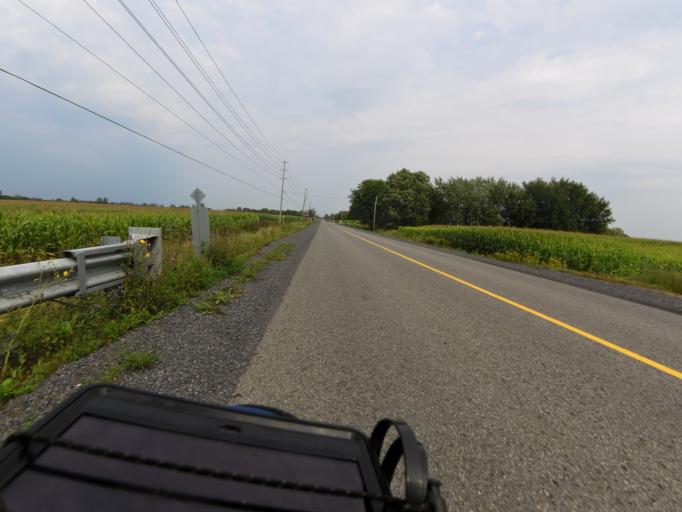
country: CA
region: Ontario
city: Casselman
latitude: 45.1912
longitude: -75.3298
